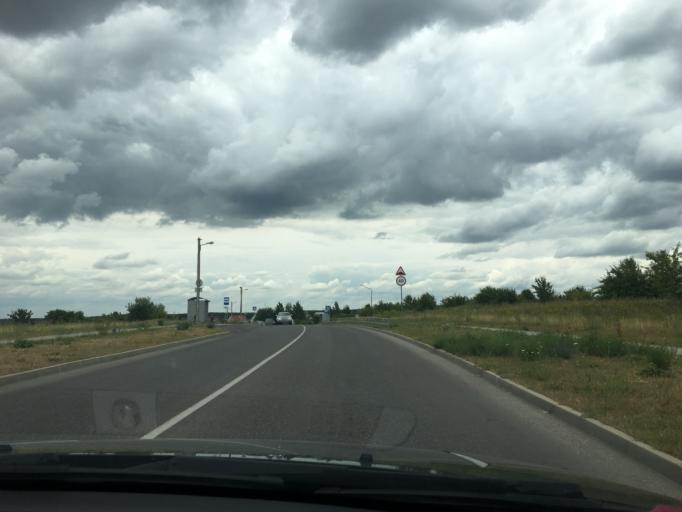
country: BY
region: Grodnenskaya
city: Hrodna
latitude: 53.6196
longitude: 23.8318
